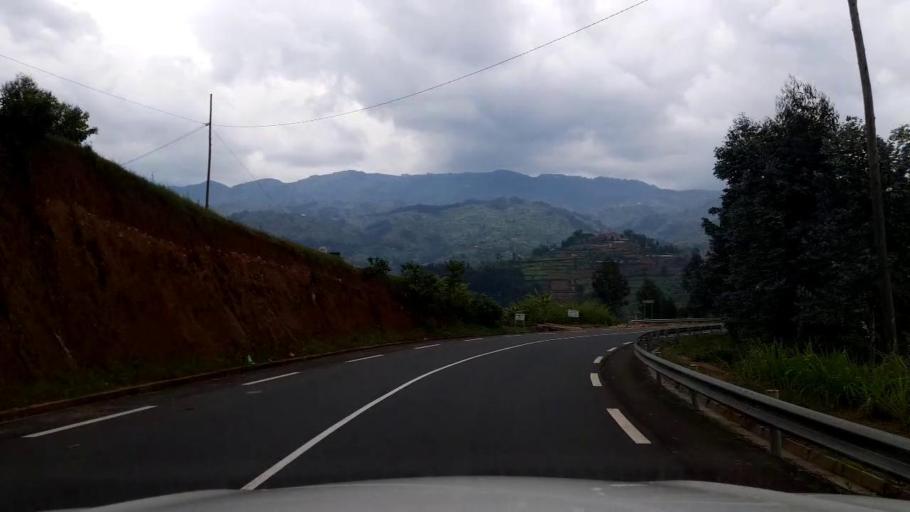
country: RW
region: Western Province
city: Kibuye
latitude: -1.9049
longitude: 29.3641
